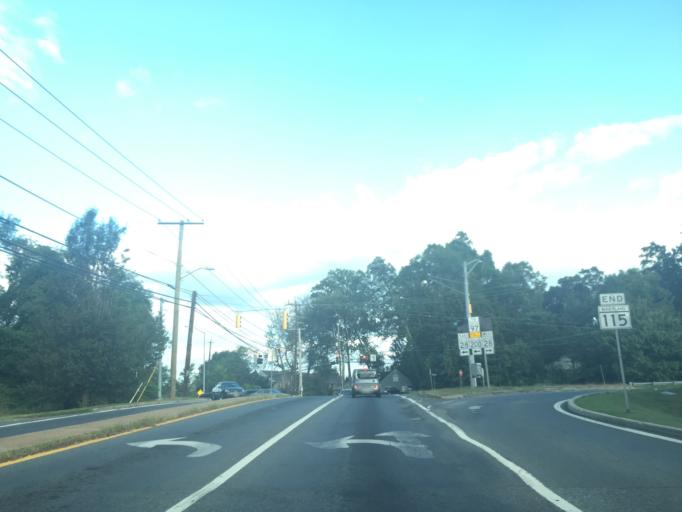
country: US
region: Maryland
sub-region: Montgomery County
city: Rossmoor
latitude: 39.1093
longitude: -77.0807
